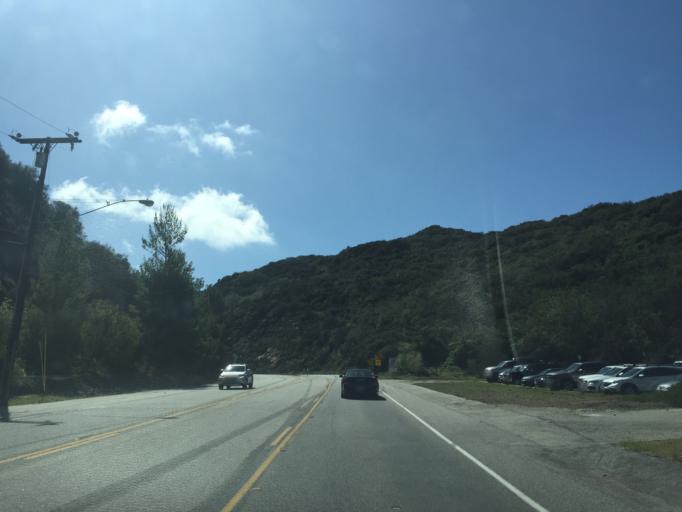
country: US
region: California
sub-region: Los Angeles County
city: Westlake Village
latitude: 34.0765
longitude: -118.8152
